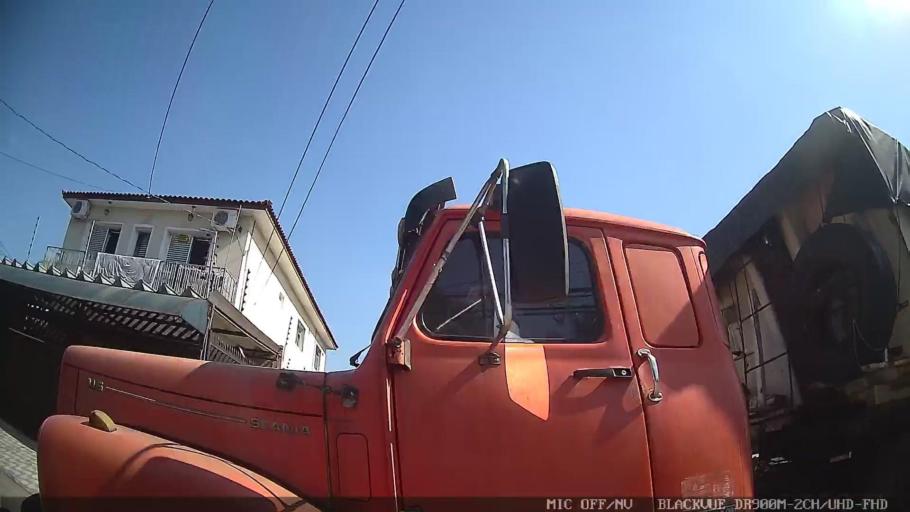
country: BR
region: Sao Paulo
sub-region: Santos
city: Santos
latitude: -23.9355
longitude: -46.3050
